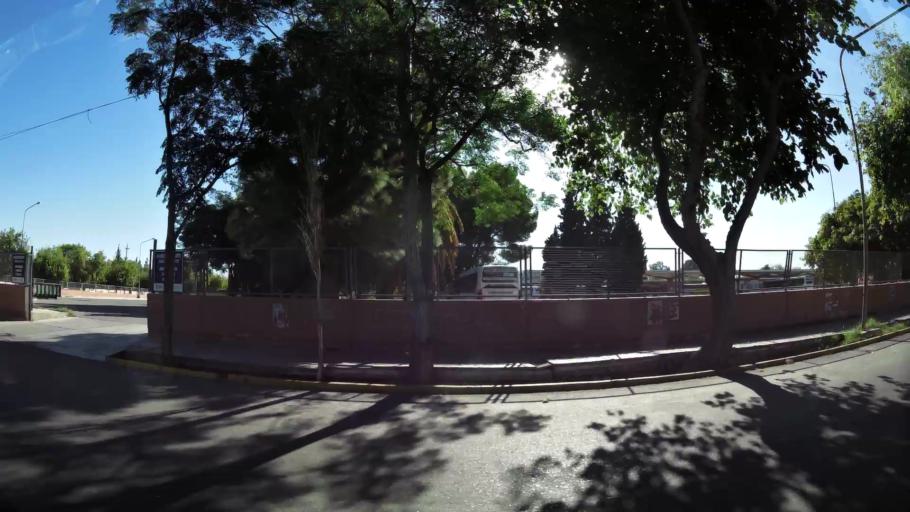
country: AR
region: San Juan
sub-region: Departamento de Santa Lucia
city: Santa Lucia
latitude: -31.5398
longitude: -68.5099
